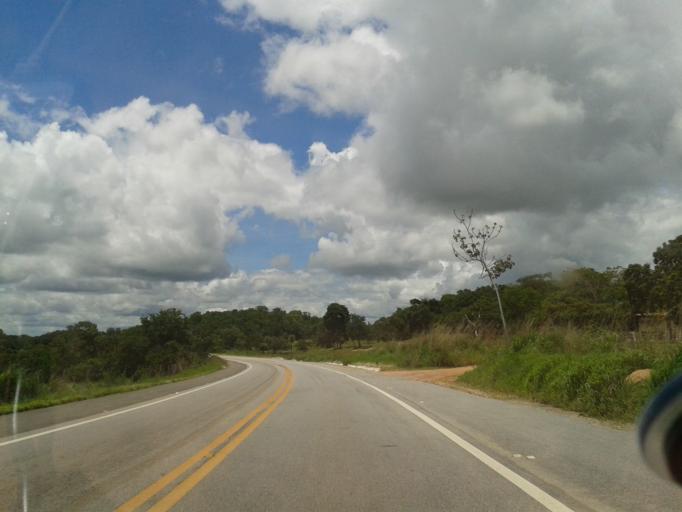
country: BR
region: Goias
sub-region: Goias
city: Goias
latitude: -15.8523
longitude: -50.0923
